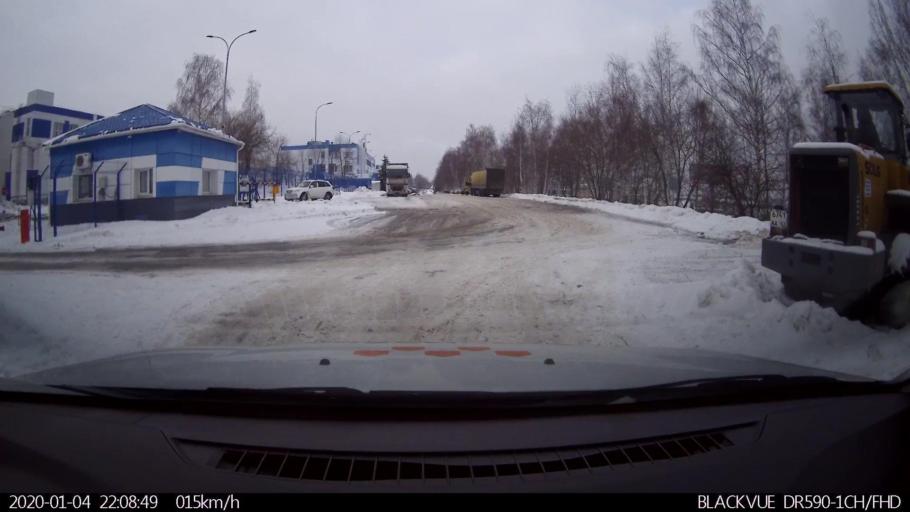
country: RU
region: Nizjnij Novgorod
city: Afonino
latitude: 56.2364
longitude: 44.0135
